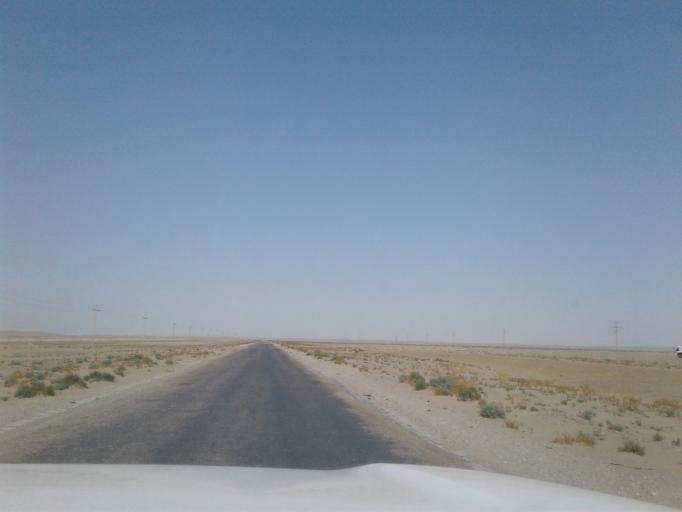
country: TM
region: Balkan
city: Gumdag
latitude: 38.3793
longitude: 54.3931
